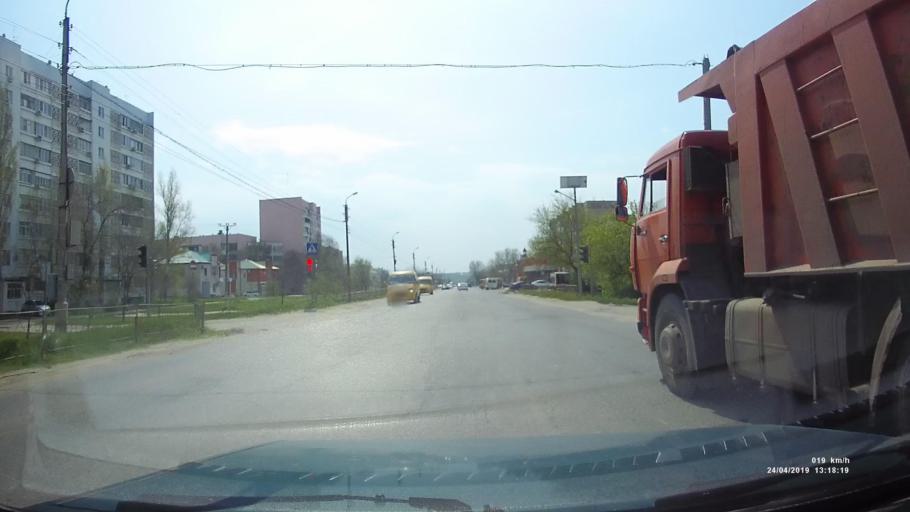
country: RU
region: Kalmykiya
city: Elista
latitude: 46.3029
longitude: 44.2950
